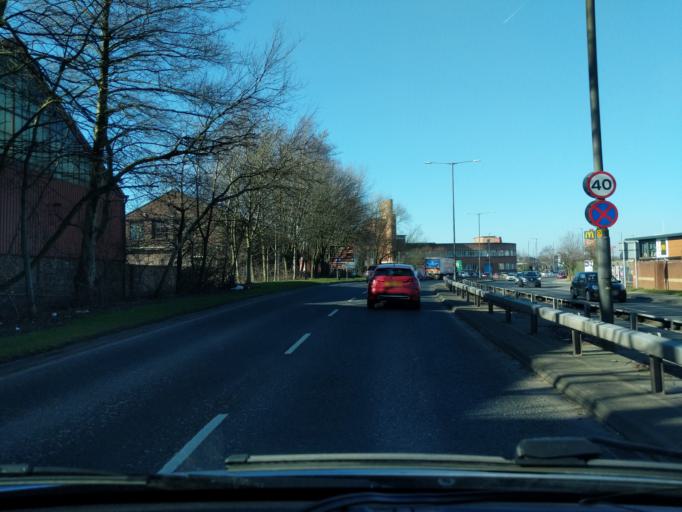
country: GB
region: England
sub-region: St. Helens
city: St Helens
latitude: 53.4495
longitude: -2.7384
